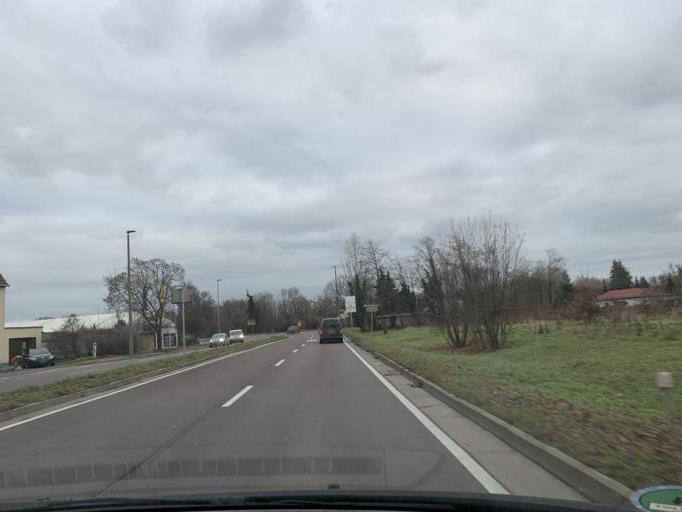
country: DE
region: Saxony-Anhalt
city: Merseburg
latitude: 51.3559
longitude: 12.0079
